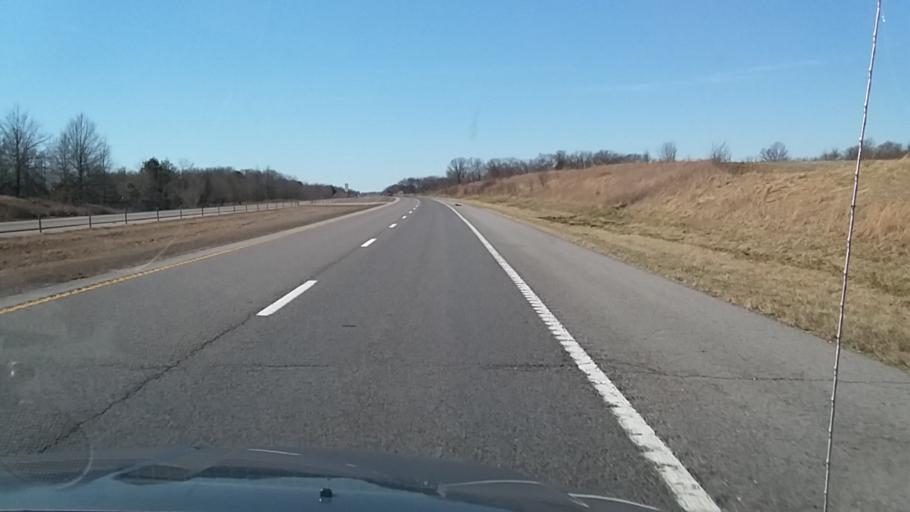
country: US
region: Missouri
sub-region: Perry County
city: Perryville
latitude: 37.5959
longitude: -89.7769
